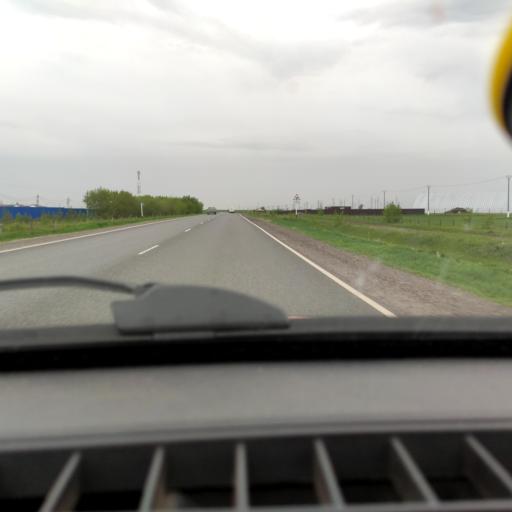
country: RU
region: Samara
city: Povolzhskiy
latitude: 53.6454
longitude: 49.6715
